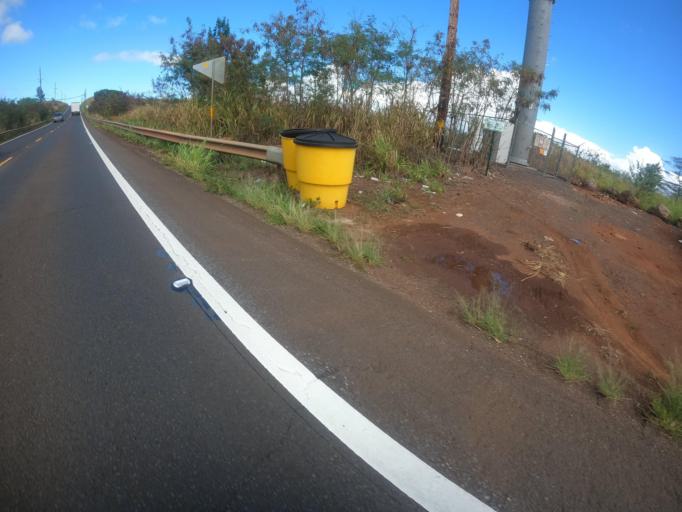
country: US
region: Hawaii
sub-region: Honolulu County
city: Waipi'o Acres
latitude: 21.4413
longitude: -158.0597
